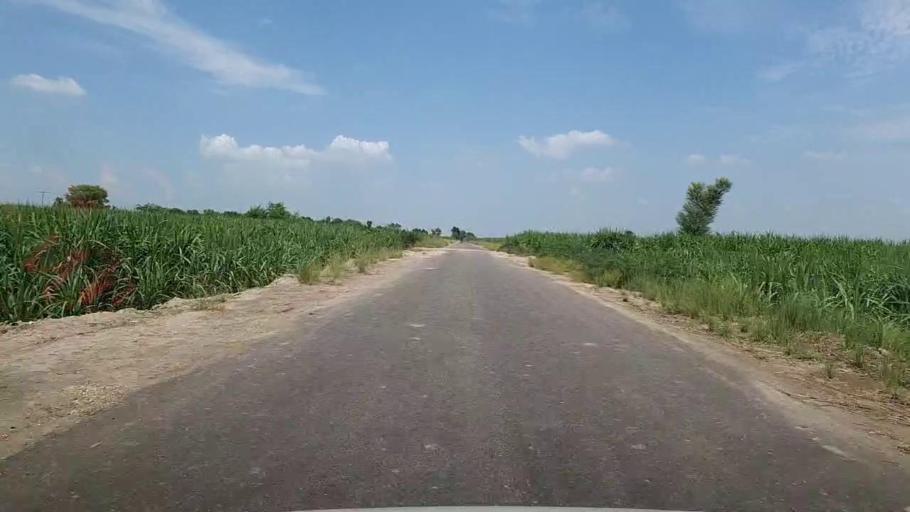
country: PK
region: Sindh
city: Bhiria
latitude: 26.9363
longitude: 68.2177
